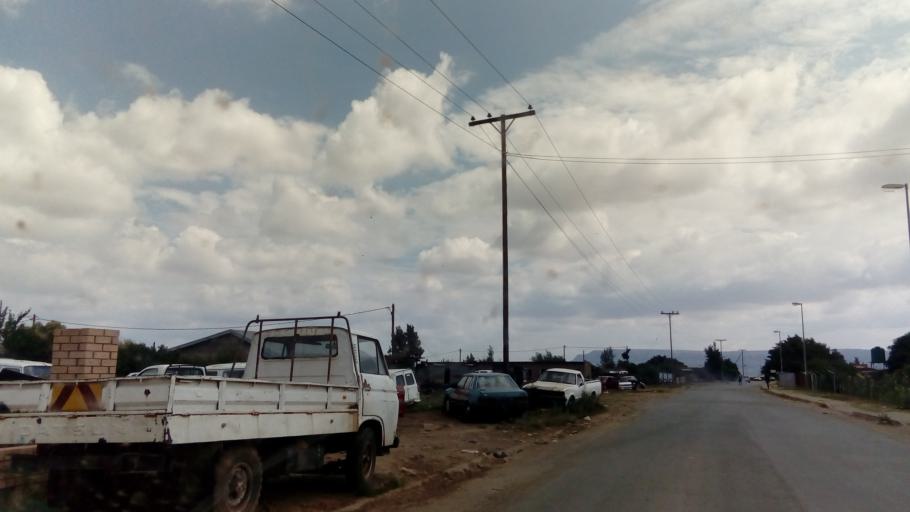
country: LS
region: Maseru
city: Maseru
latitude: -29.3810
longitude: 27.5303
